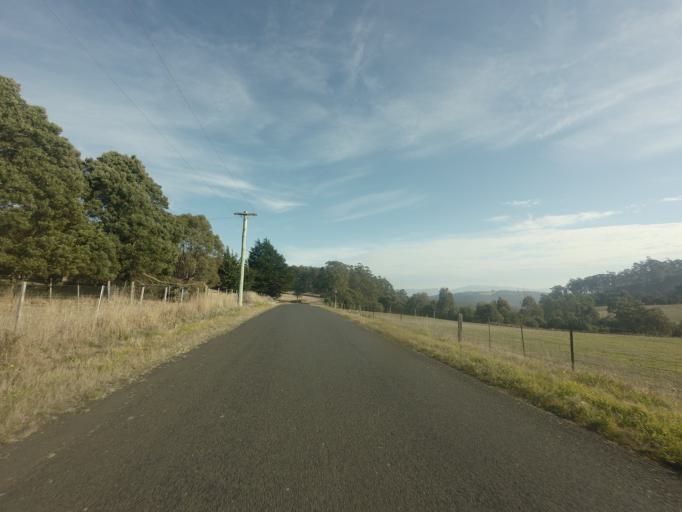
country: AU
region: Tasmania
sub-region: Sorell
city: Sorell
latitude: -42.4814
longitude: 147.4560
